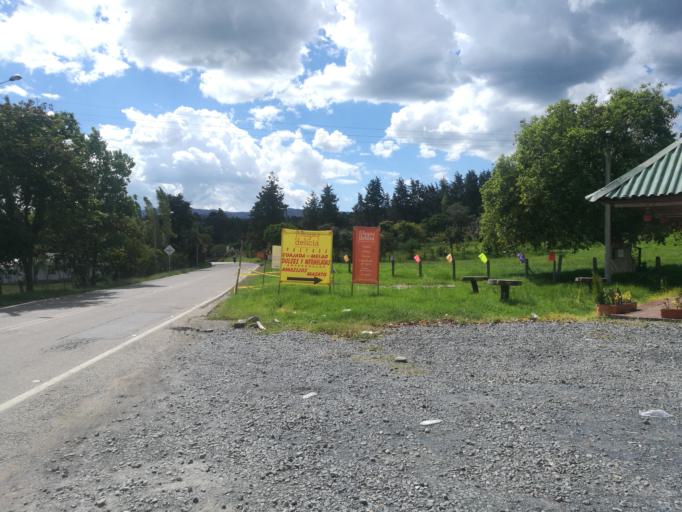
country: CO
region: Boyaca
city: Raquira
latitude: 5.5717
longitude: -73.6533
